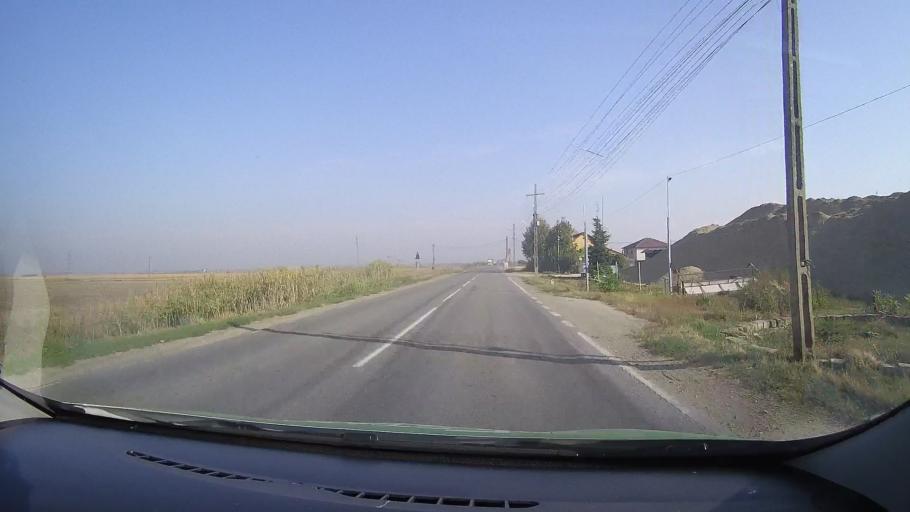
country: RO
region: Arad
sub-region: Comuna Pilu
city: Pilu
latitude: 46.5838
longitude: 21.3440
